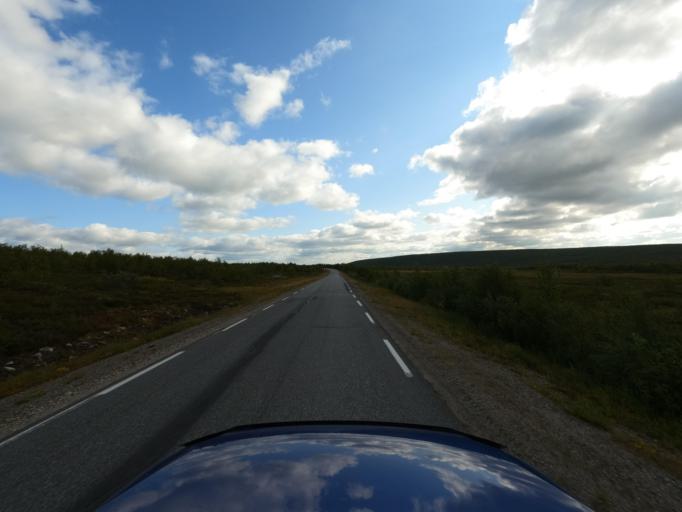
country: NO
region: Finnmark Fylke
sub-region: Porsanger
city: Lakselv
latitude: 69.3738
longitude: 24.4084
